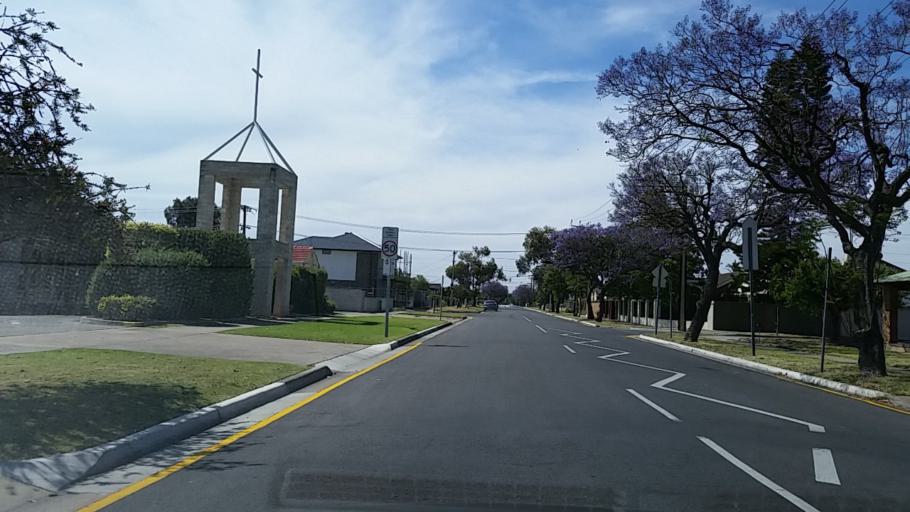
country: AU
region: South Australia
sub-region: Charles Sturt
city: Albert Park
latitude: -34.8804
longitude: 138.5215
